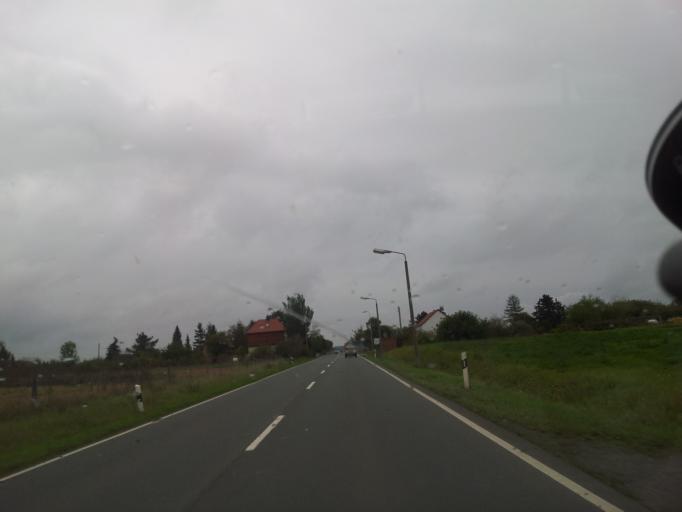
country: DE
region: Saxony-Anhalt
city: Timmenrode
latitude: 51.7963
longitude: 10.9884
